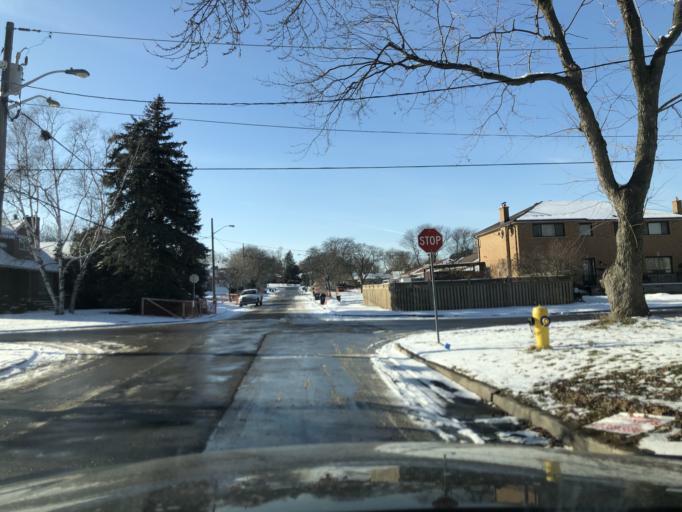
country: CA
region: Ontario
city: Etobicoke
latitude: 43.7077
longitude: -79.5190
